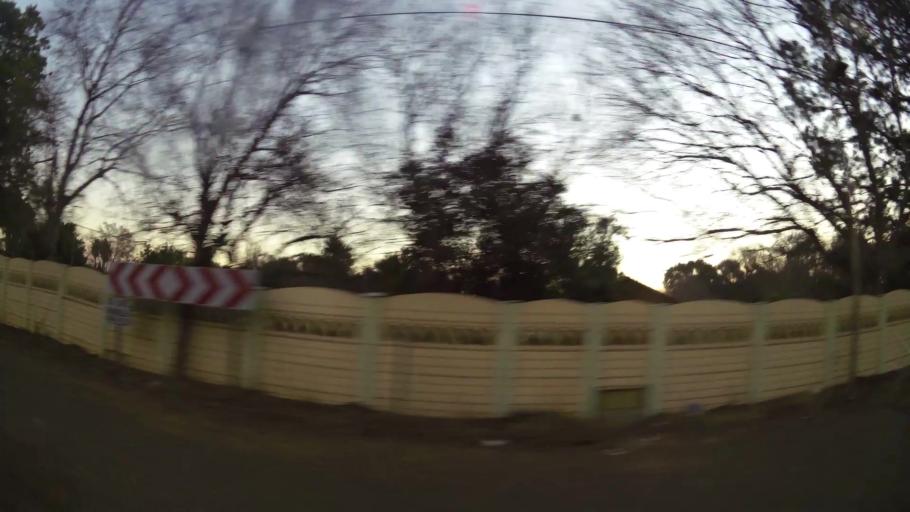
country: ZA
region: Gauteng
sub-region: City of Tshwane Metropolitan Municipality
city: Centurion
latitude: -25.8541
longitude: 28.1334
